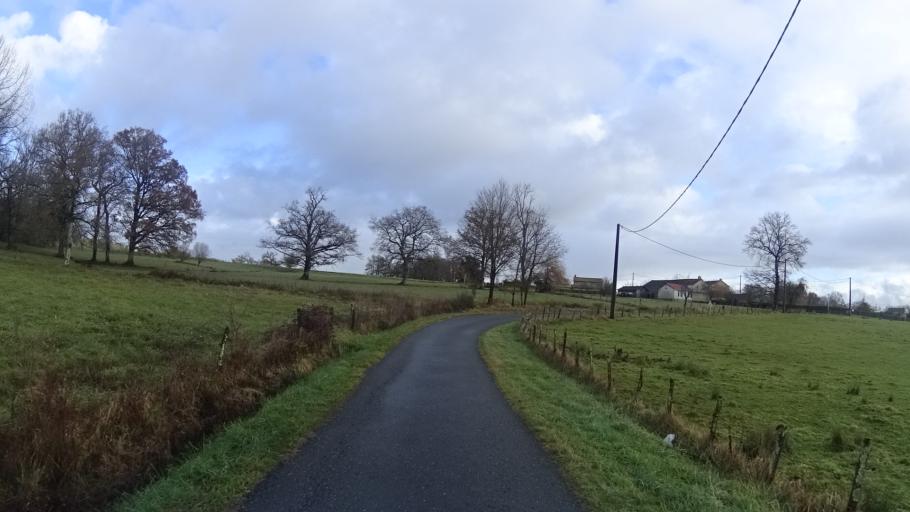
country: FR
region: Aquitaine
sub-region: Departement de la Dordogne
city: Thiviers
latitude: 45.4030
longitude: 0.9564
